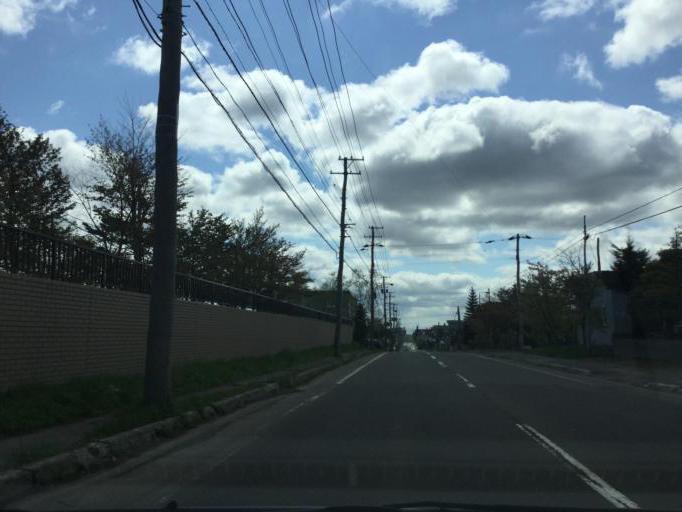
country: JP
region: Hokkaido
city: Iwamizawa
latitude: 43.2145
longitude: 141.7963
